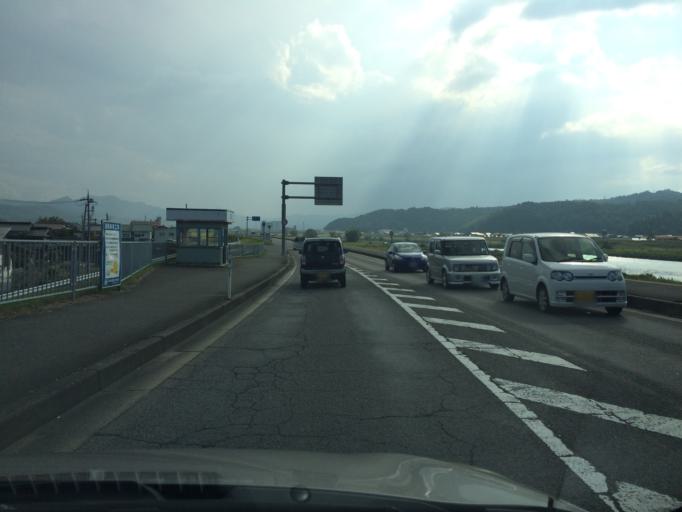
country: JP
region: Hyogo
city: Toyooka
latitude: 35.5261
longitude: 134.8273
